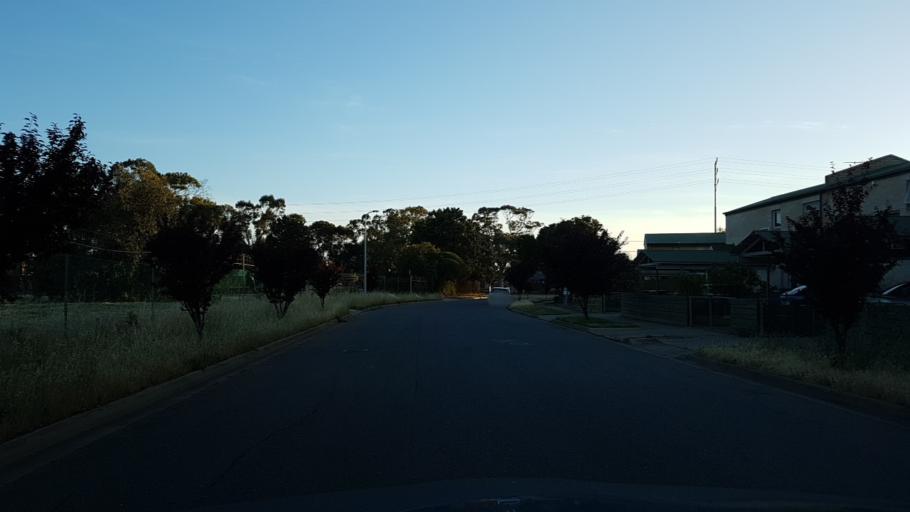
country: AU
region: South Australia
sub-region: Charles Sturt
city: Woodville North
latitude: -34.8651
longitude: 138.5341
